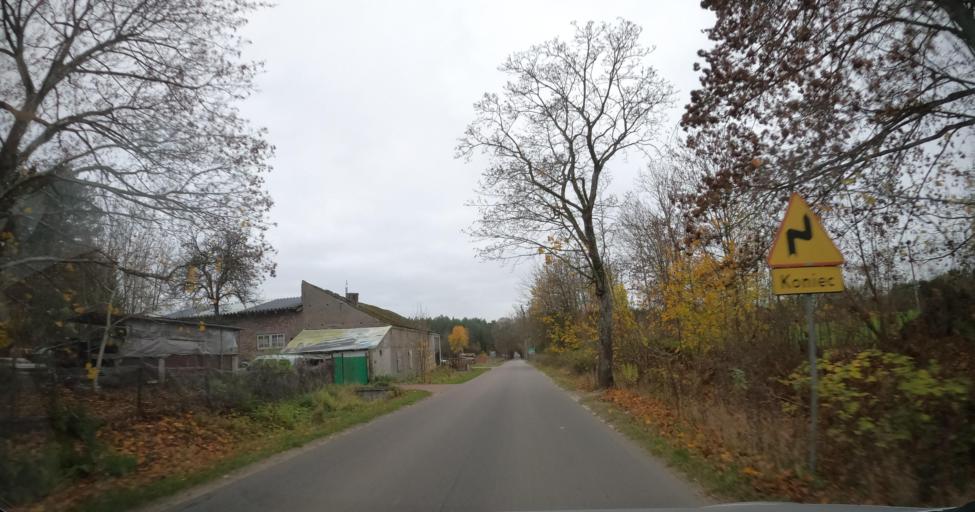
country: PL
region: West Pomeranian Voivodeship
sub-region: Powiat swidwinski
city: Polczyn-Zdroj
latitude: 53.7751
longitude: 16.1605
